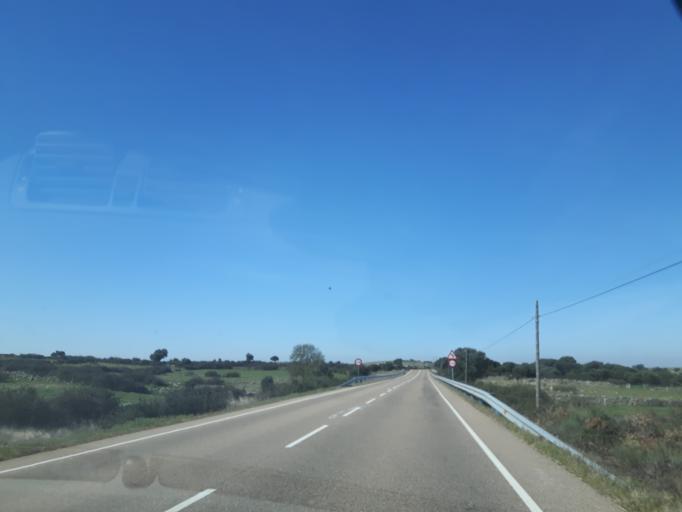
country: ES
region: Castille and Leon
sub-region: Provincia de Salamanca
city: Guadramiro
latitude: 41.0114
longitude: -6.4877
